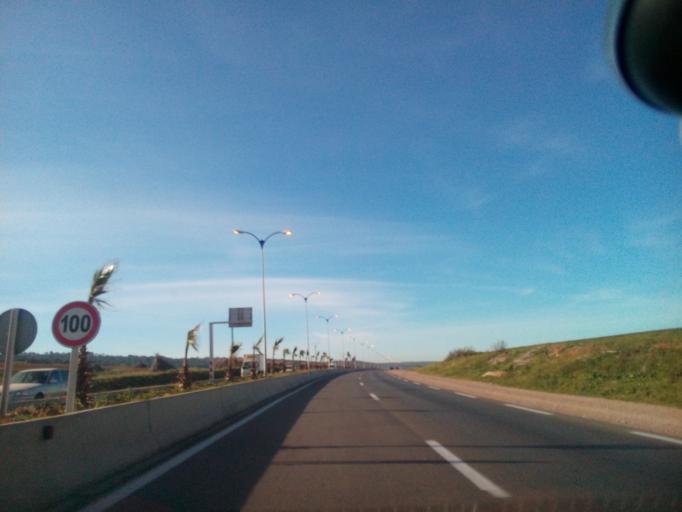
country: DZ
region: Mostaganem
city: Mostaganem
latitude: 35.8226
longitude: -0.0153
